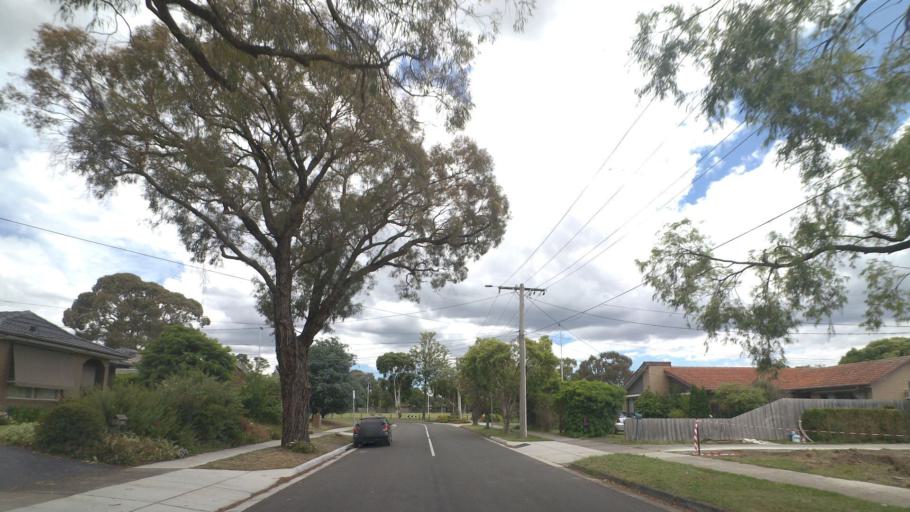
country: AU
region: Victoria
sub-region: Maroondah
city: Heathmont
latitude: -37.8475
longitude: 145.2380
